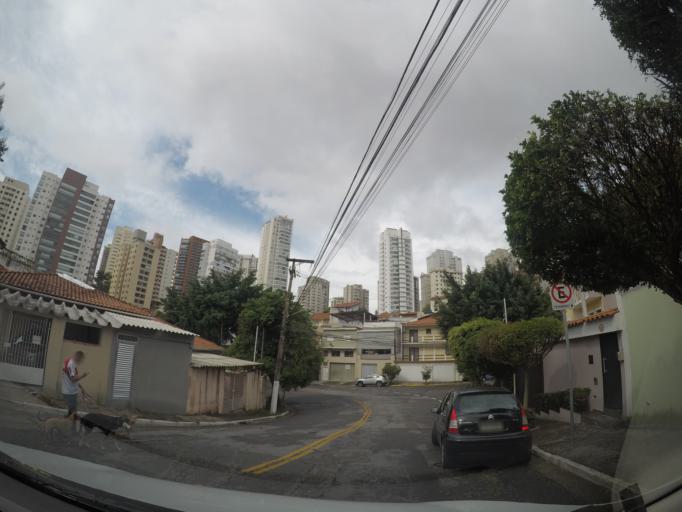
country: BR
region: Sao Paulo
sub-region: Sao Paulo
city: Sao Paulo
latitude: -23.5881
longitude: -46.6251
